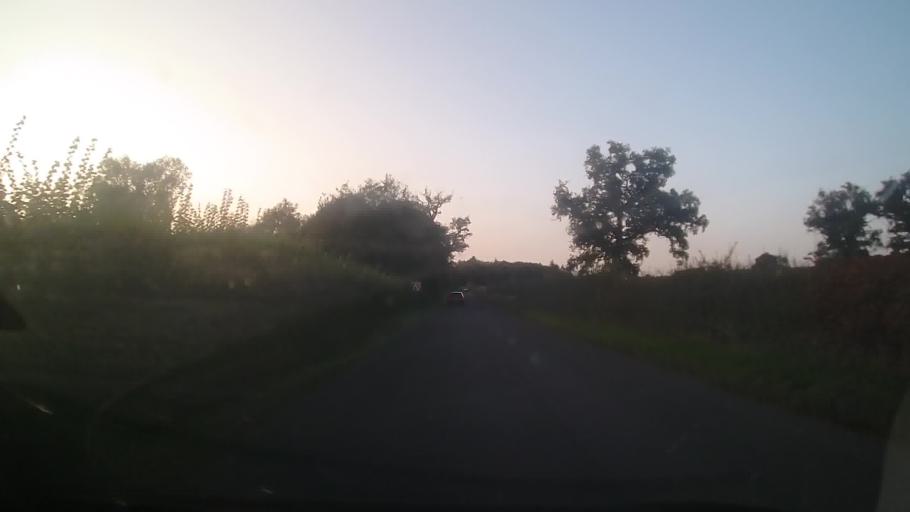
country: GB
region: England
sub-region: Shropshire
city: Bicton
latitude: 52.7645
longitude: -2.7988
